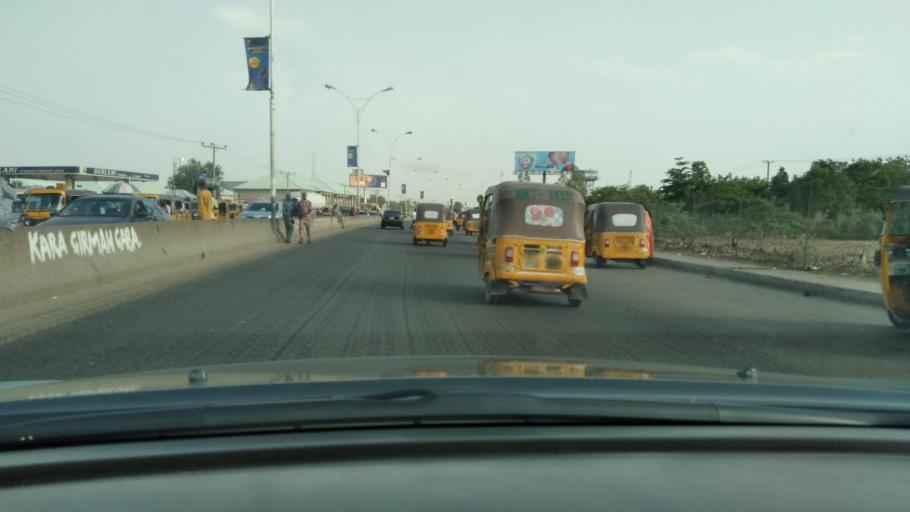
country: NG
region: Kano
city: Kano
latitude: 11.9505
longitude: 8.5652
